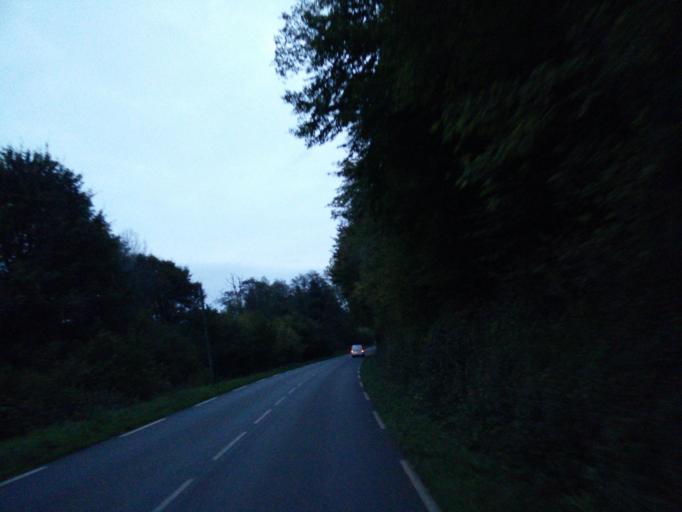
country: FR
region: Aquitaine
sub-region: Departement de la Dordogne
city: Saint-Cyprien
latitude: 44.9428
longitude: 1.0339
